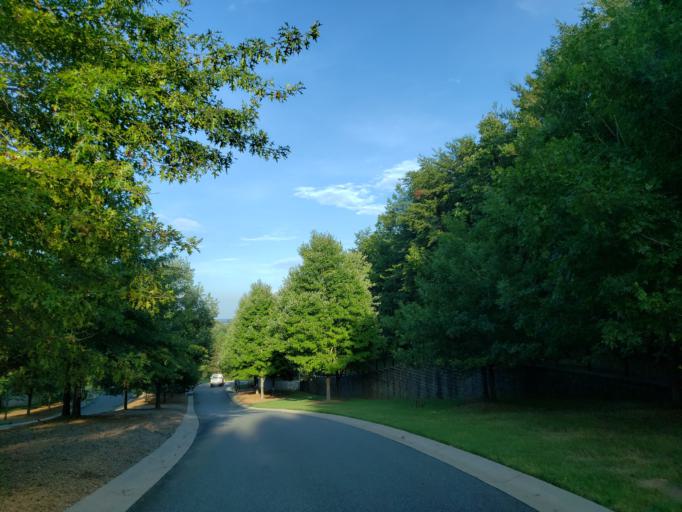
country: US
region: Georgia
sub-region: Cherokee County
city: Canton
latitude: 34.2334
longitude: -84.5753
